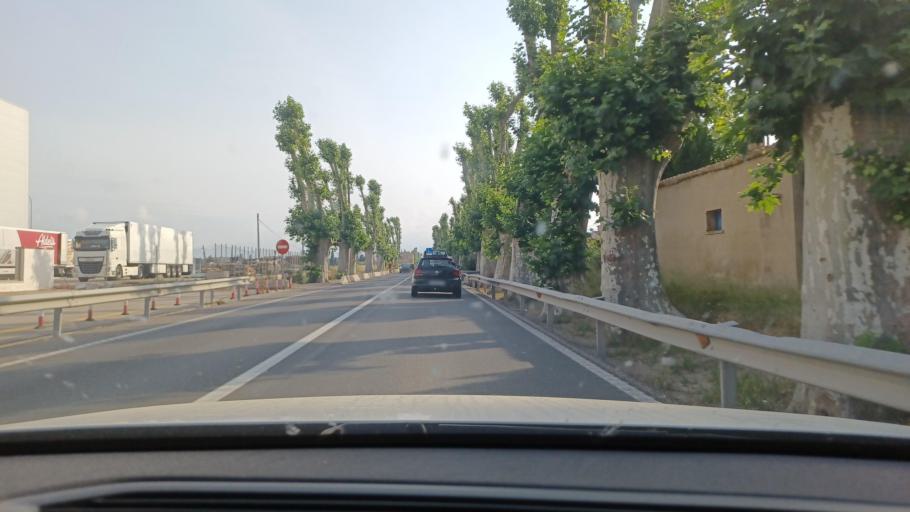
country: ES
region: Catalonia
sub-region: Provincia de Tarragona
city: Tortosa
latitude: 40.7970
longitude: 0.4990
